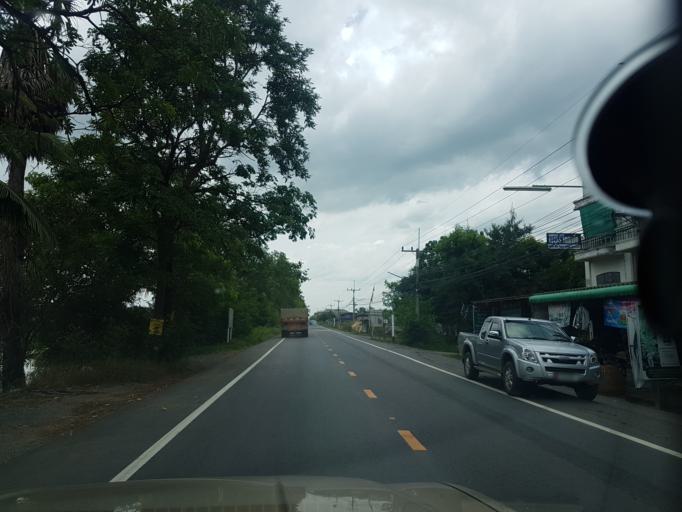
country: TH
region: Sara Buri
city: Nong Khae
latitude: 14.2788
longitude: 100.8918
